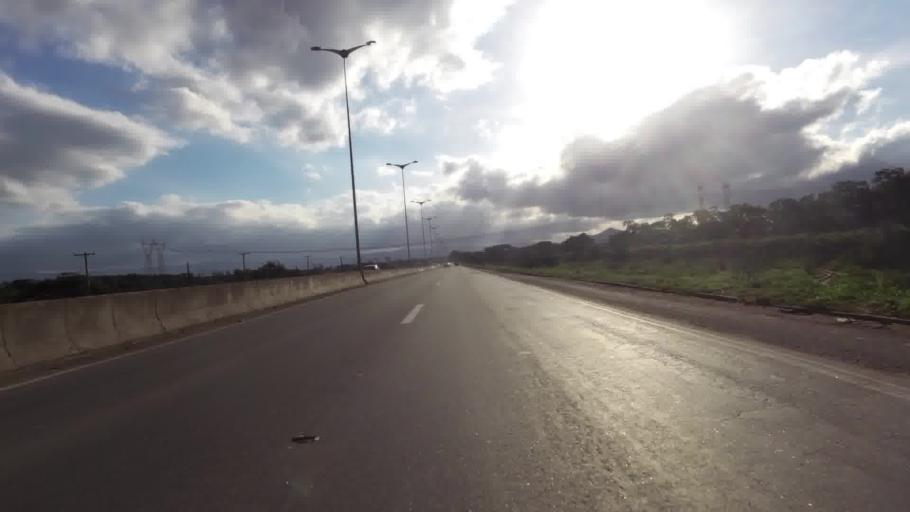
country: BR
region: Espirito Santo
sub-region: Serra
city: Serra
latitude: -20.2085
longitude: -40.3029
